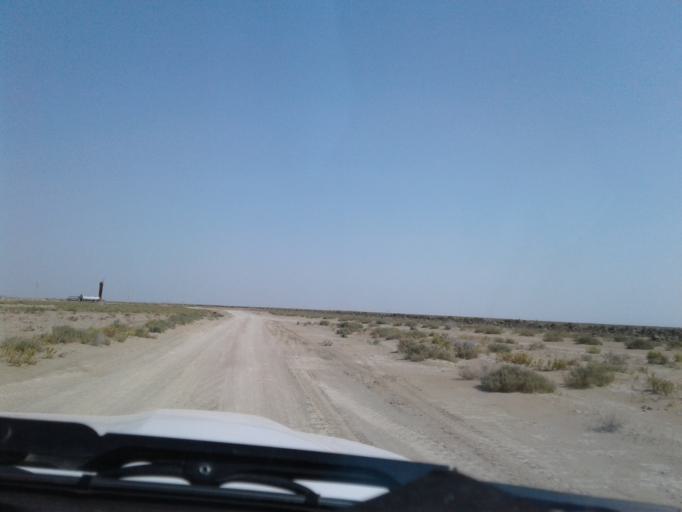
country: IR
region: Golestan
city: Gomishan
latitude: 37.8172
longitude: 53.9219
